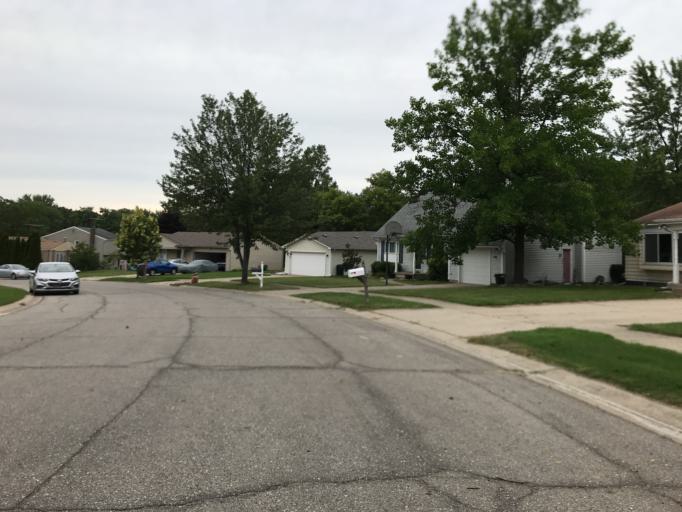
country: US
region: Michigan
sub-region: Oakland County
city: South Lyon
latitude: 42.4648
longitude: -83.6401
